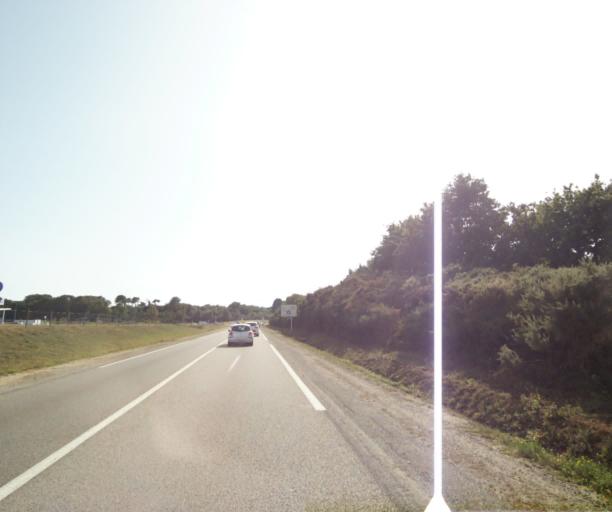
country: FR
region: Brittany
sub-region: Departement du Morbihan
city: Riantec
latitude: 47.7275
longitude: -3.3217
